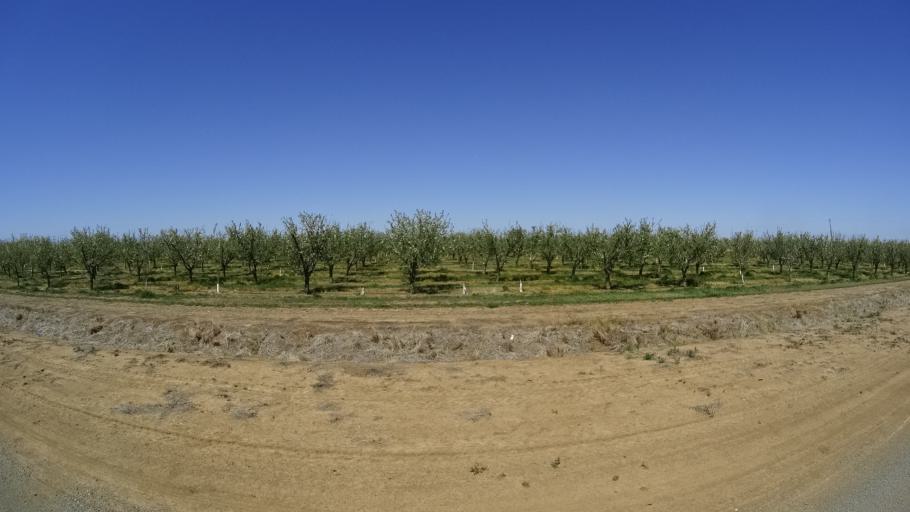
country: US
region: California
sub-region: Glenn County
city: Willows
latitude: 39.4802
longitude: -122.2785
